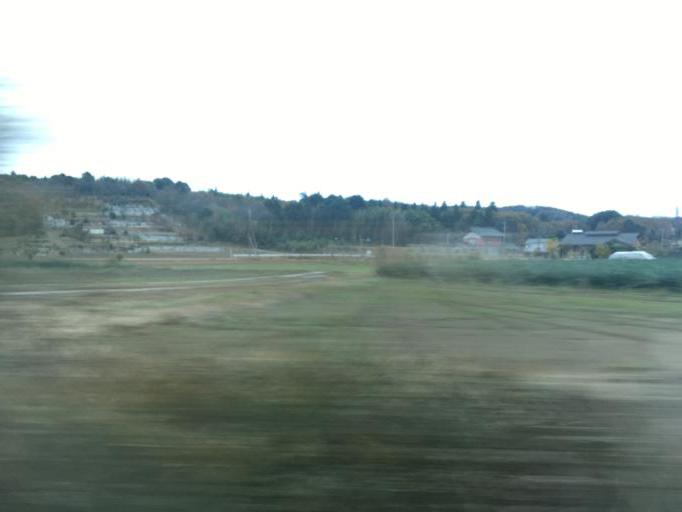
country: JP
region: Ibaraki
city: Iwase
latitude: 36.3534
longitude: 140.0885
